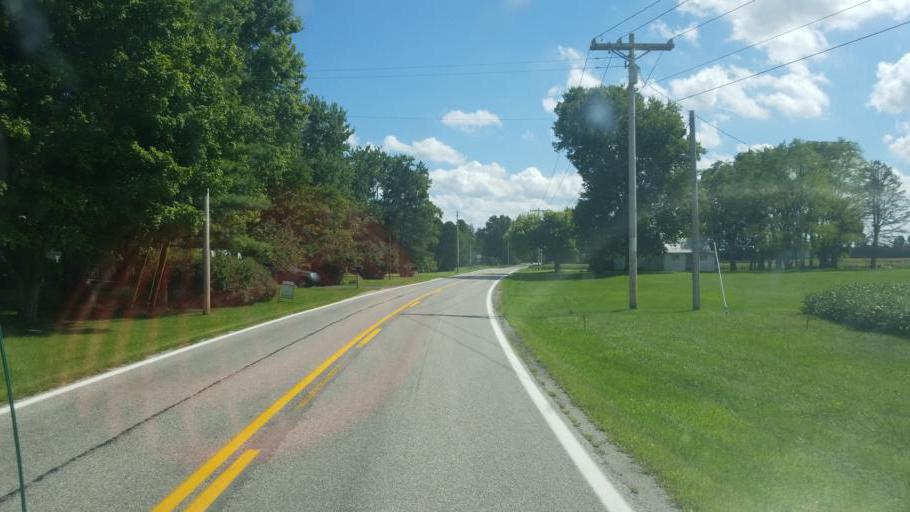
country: US
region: Ohio
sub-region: Marion County
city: Prospect
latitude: 40.3624
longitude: -83.1856
